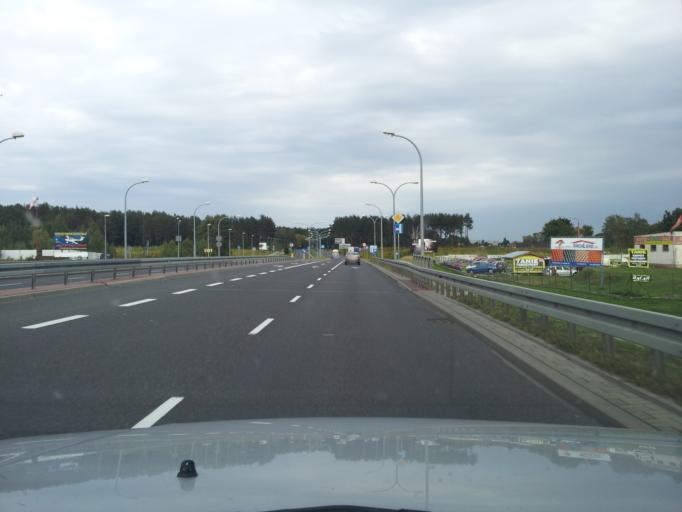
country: PL
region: Warmian-Masurian Voivodeship
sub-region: Olsztyn
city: Kortowo
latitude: 53.7691
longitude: 20.4205
